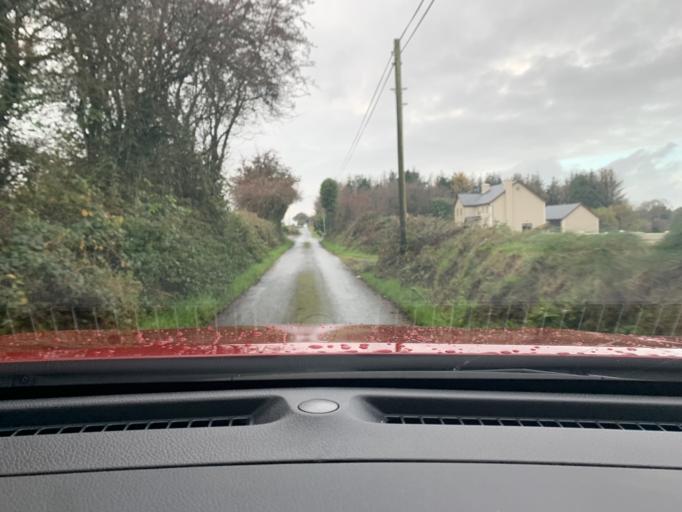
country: IE
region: Connaught
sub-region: Roscommon
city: Ballaghaderreen
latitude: 53.9667
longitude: -8.5672
